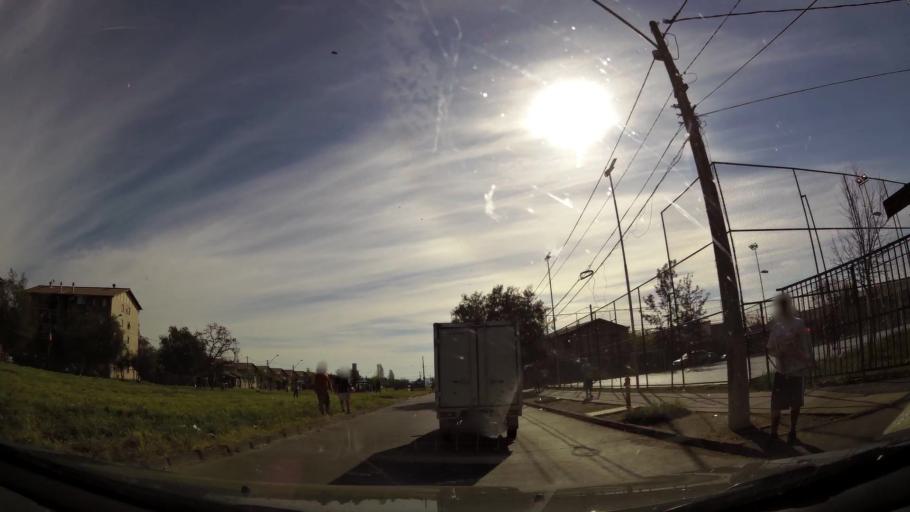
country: CL
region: Santiago Metropolitan
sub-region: Provincia de Cordillera
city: Puente Alto
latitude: -33.6316
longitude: -70.5918
